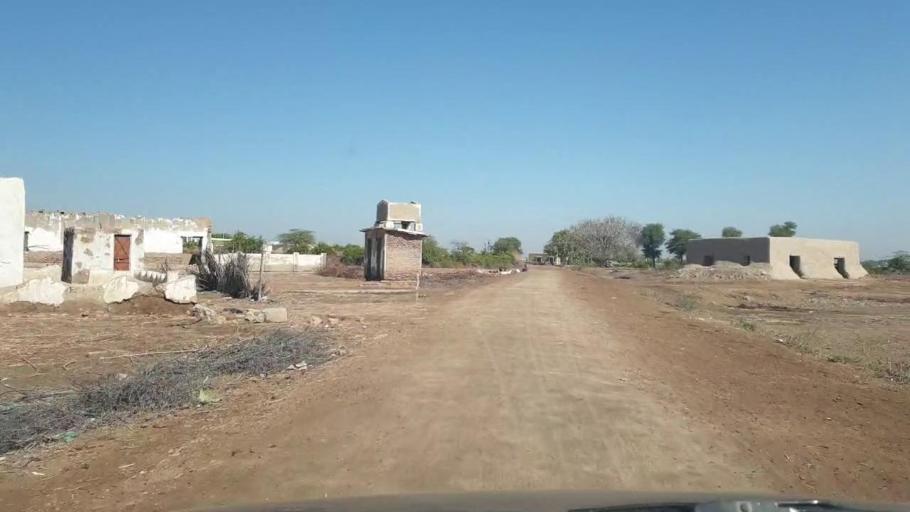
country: PK
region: Sindh
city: Umarkot
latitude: 25.3926
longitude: 69.6941
